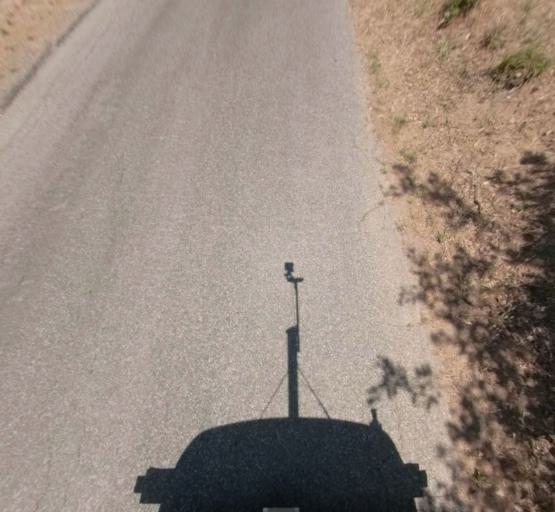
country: US
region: California
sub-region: Fresno County
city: Auberry
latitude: 37.2337
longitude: -119.4609
